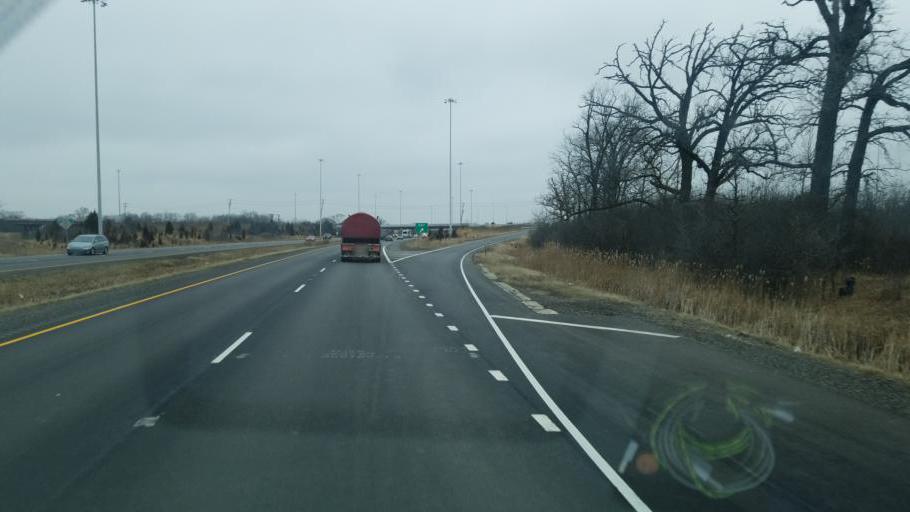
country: US
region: Illinois
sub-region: Lake County
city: Park City
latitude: 42.3448
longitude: -87.8902
